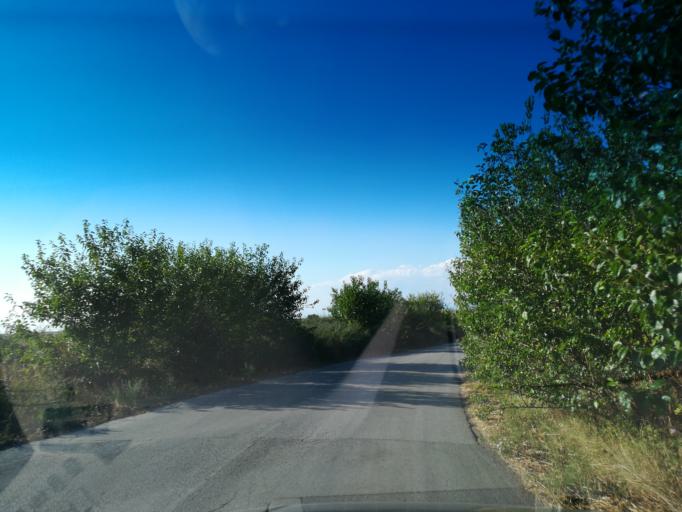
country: BG
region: Khaskovo
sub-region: Obshtina Mineralni Bani
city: Mineralni Bani
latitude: 42.0520
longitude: 25.2710
